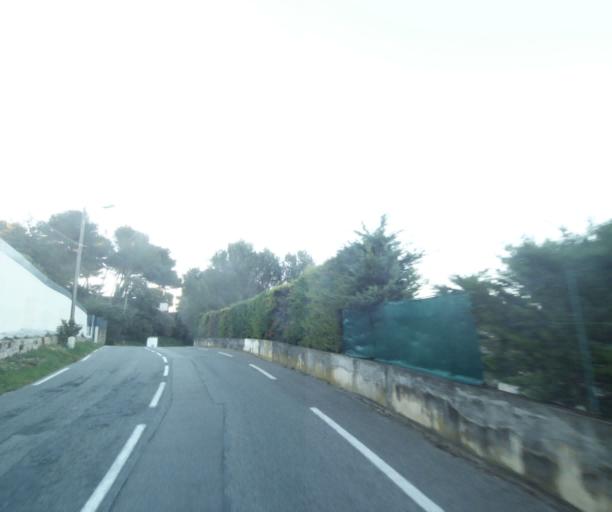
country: FR
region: Provence-Alpes-Cote d'Azur
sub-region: Departement des Alpes-Maritimes
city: Vallauris
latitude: 43.5847
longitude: 7.0814
